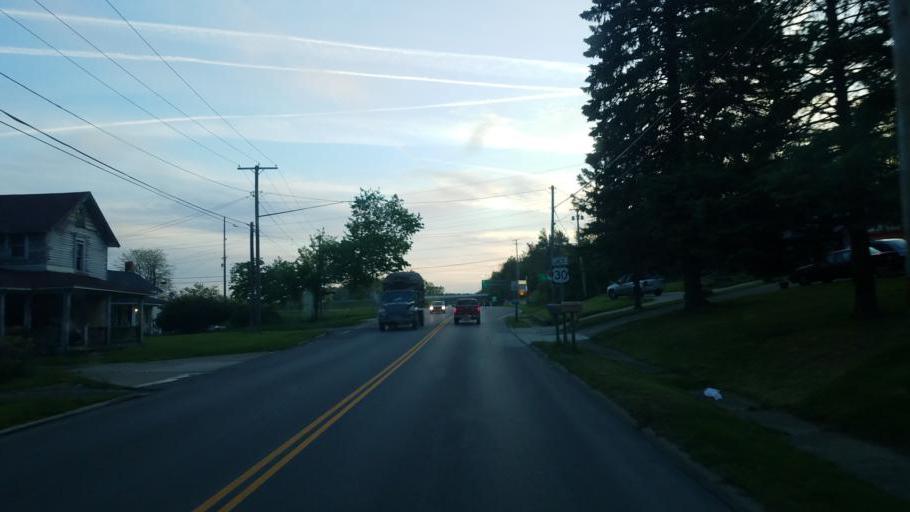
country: US
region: Ohio
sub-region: Richland County
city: Mansfield
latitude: 40.7760
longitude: -82.5057
